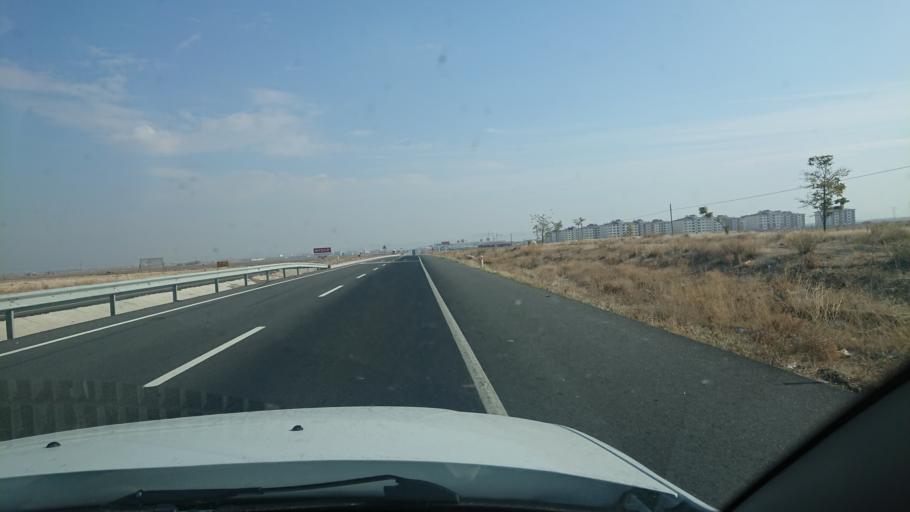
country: TR
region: Aksaray
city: Yesilova
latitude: 38.3309
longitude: 33.9102
